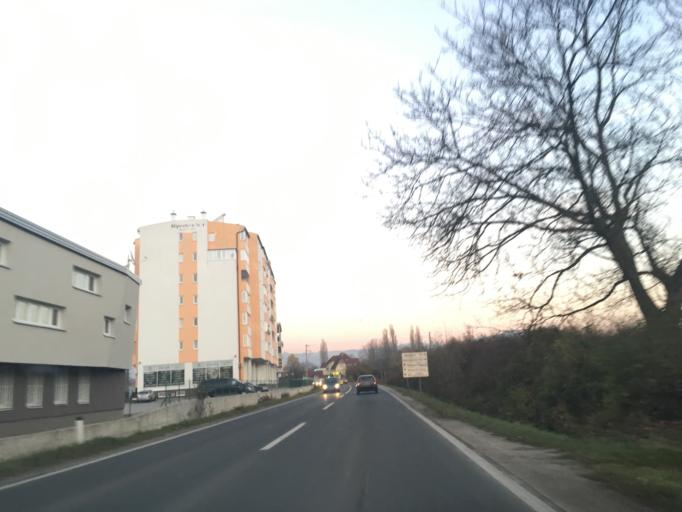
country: BA
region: Federation of Bosnia and Herzegovina
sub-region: Kanton Sarajevo
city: Sarajevo
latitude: 43.8307
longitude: 18.2917
